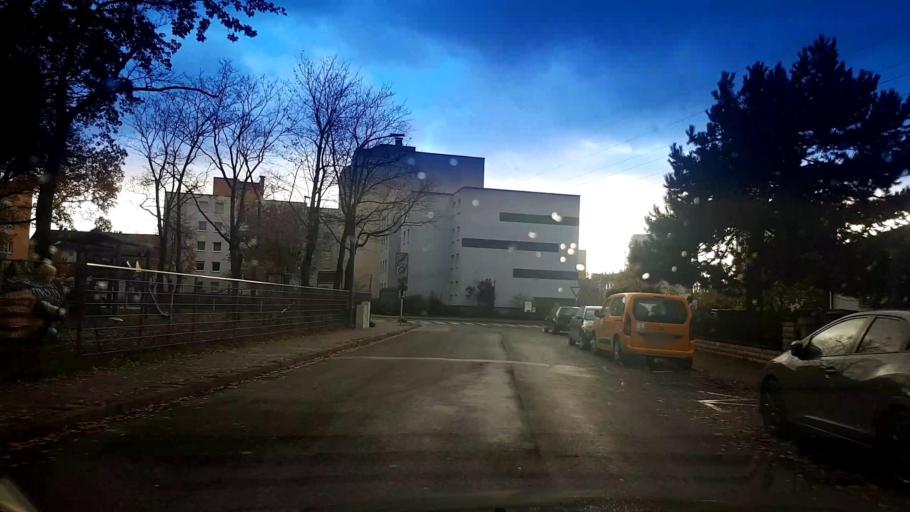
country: DE
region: Bavaria
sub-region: Upper Franconia
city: Bamberg
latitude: 49.8956
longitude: 10.9241
